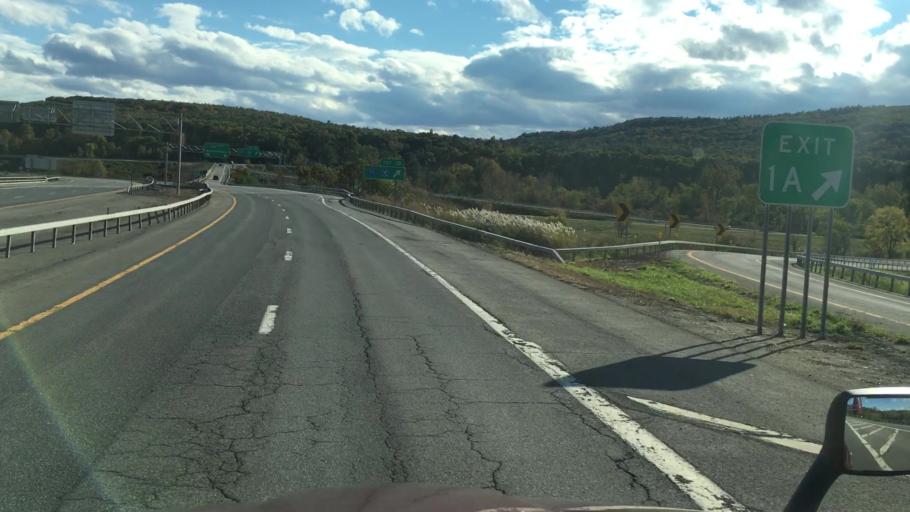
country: US
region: New York
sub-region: Schenectady County
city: Scotia
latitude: 42.8466
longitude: -74.0066
